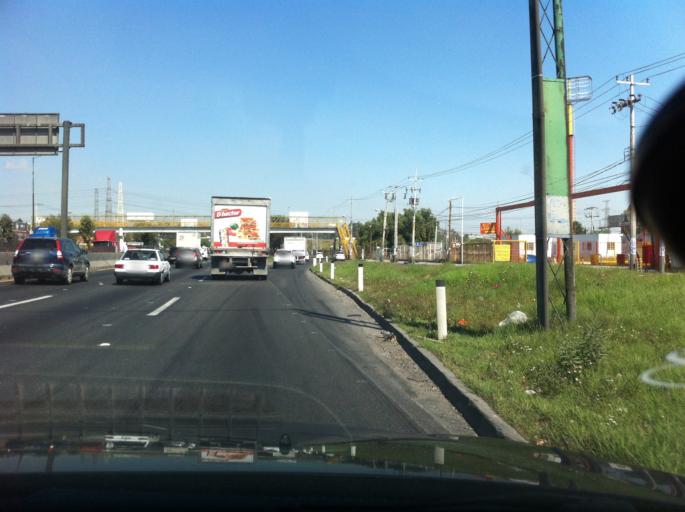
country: MX
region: Mexico
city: Cuautitlan Izcalli
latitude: 19.6316
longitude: -99.1935
